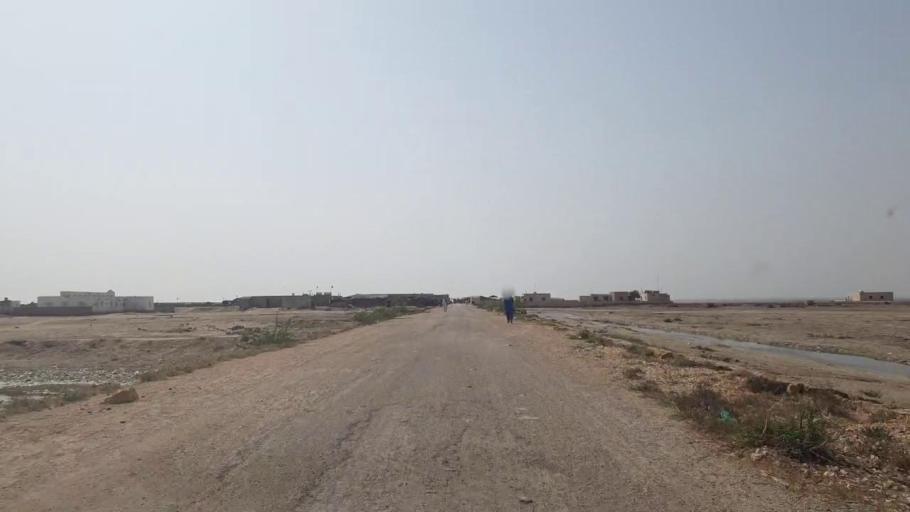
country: PK
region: Sindh
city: Jati
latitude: 24.3381
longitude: 68.5931
